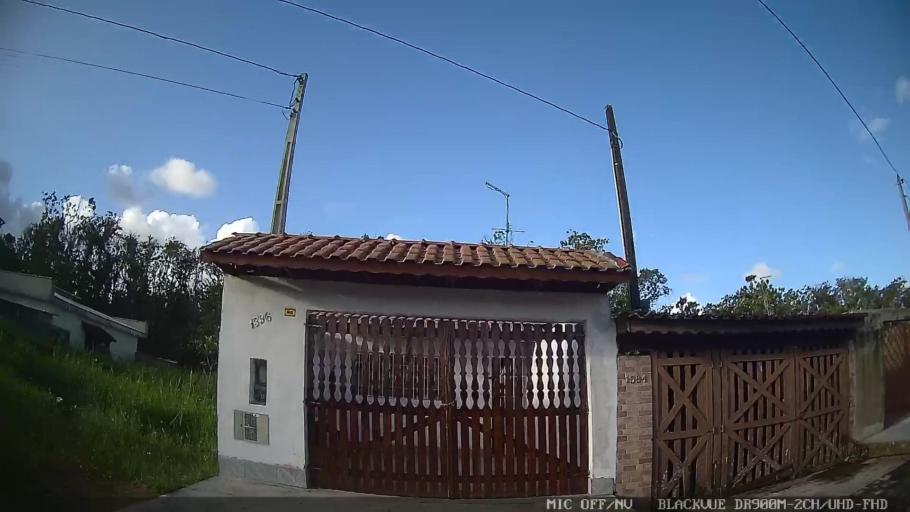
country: BR
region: Sao Paulo
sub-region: Itanhaem
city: Itanhaem
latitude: -24.1362
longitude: -46.7234
